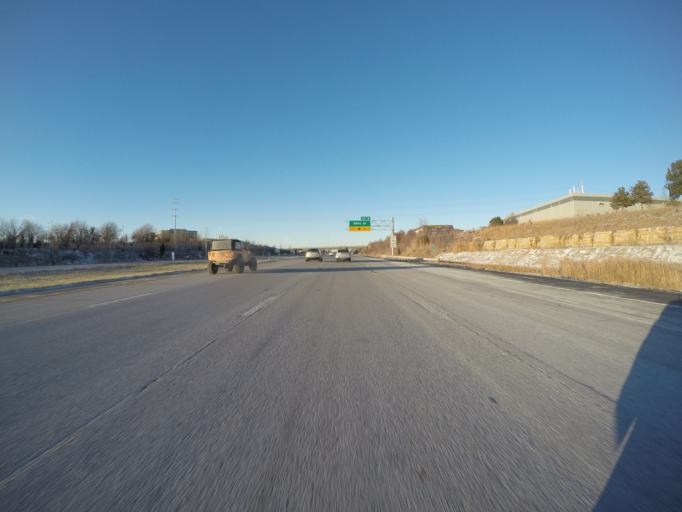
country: US
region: Kansas
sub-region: Johnson County
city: Lenexa
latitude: 38.9531
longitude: -94.7739
